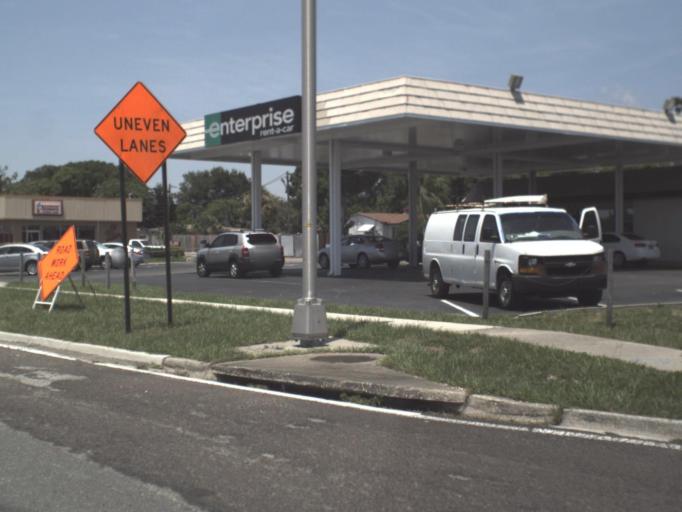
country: US
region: Florida
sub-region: Pasco County
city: New Port Richey
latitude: 28.2389
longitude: -82.7275
